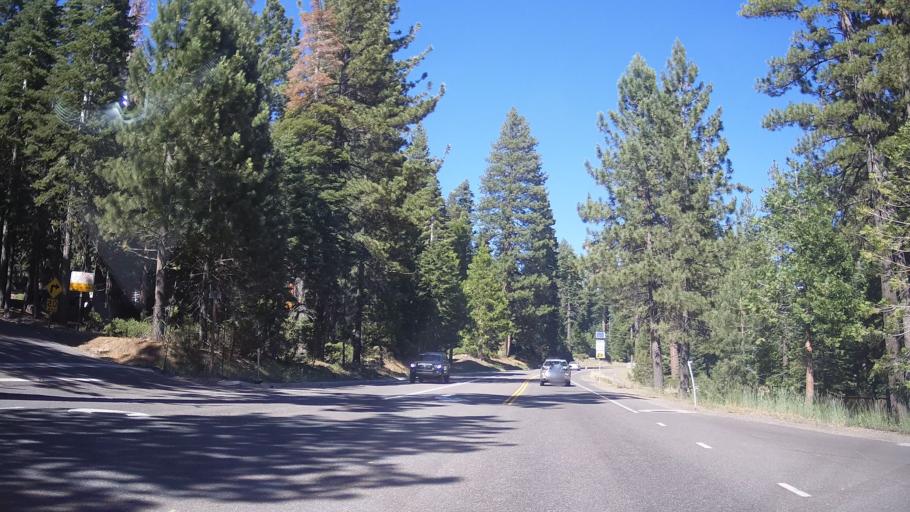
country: US
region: California
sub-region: Placer County
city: Sunnyside-Tahoe City
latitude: 39.1454
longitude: -120.1528
